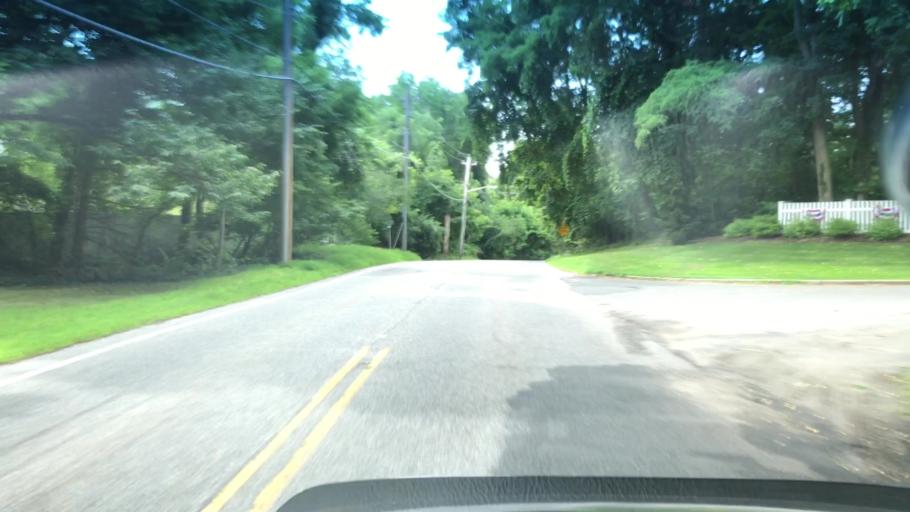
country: US
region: New York
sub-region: Suffolk County
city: Wading River
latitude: 40.9490
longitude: -72.8571
